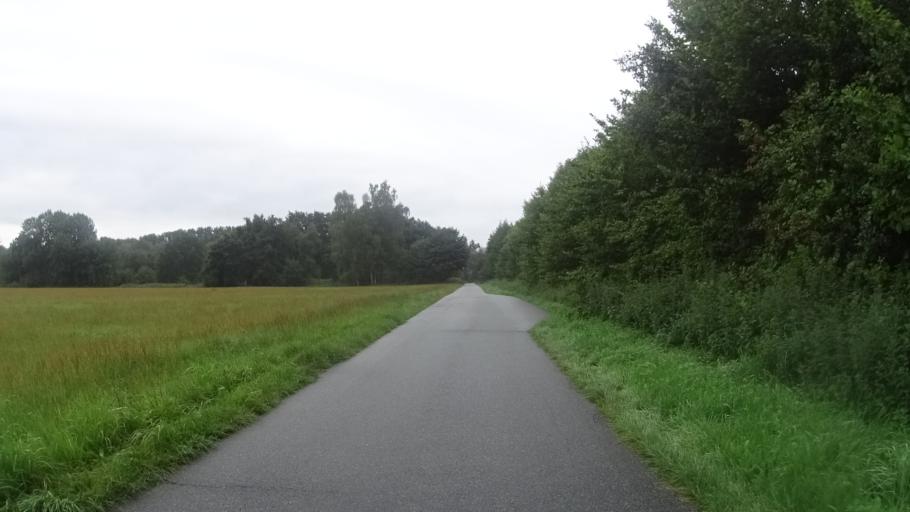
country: DE
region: Schleswig-Holstein
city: Buchen
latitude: 53.4946
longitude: 10.6223
